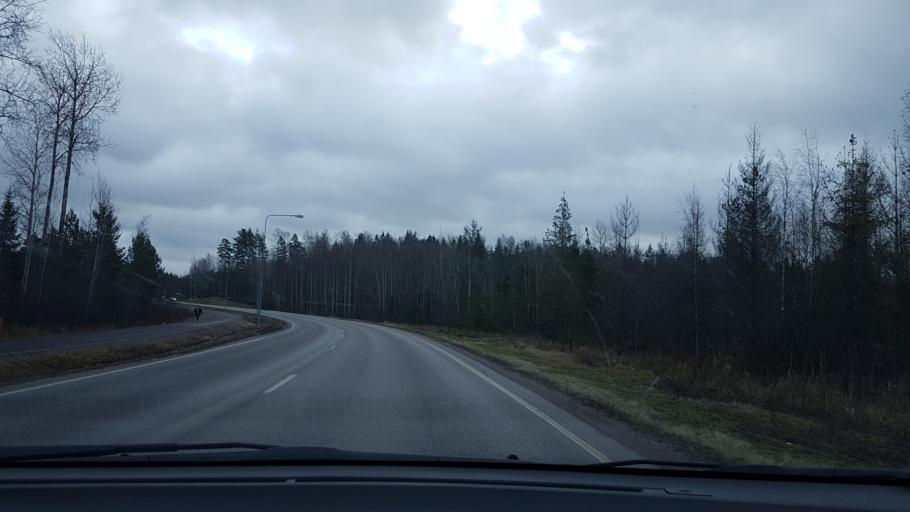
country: FI
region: Uusimaa
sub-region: Helsinki
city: Tuusula
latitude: 60.3721
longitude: 25.0636
